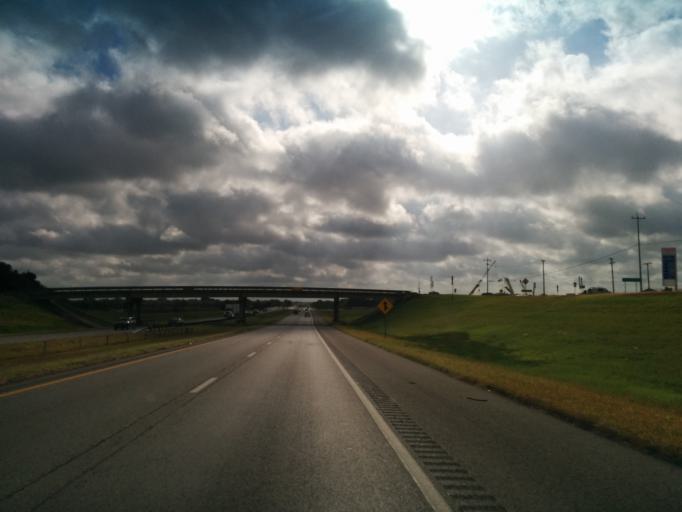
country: US
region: Texas
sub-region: Guadalupe County
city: Cibolo
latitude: 29.4971
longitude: -98.1964
